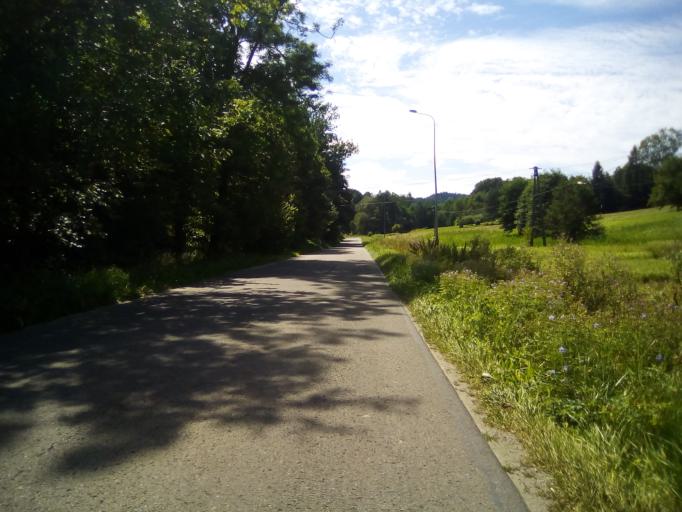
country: PL
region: Subcarpathian Voivodeship
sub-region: Powiat strzyzowski
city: Konieczkowa
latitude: 49.8291
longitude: 21.9294
